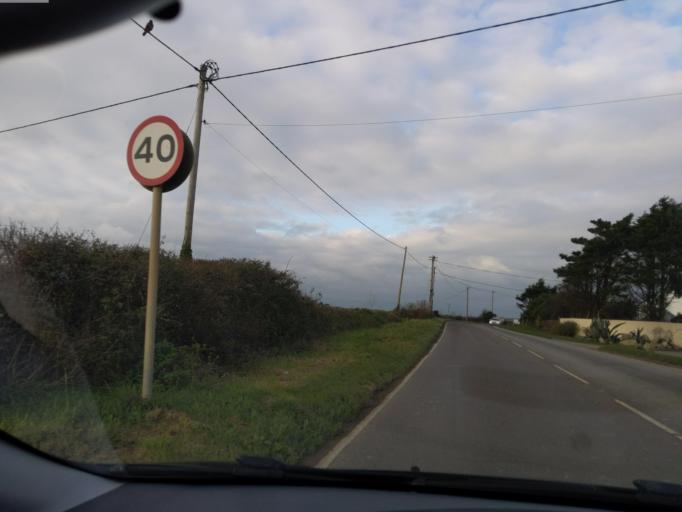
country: GB
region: England
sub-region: Cornwall
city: Padstow
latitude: 50.5242
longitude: -4.9527
